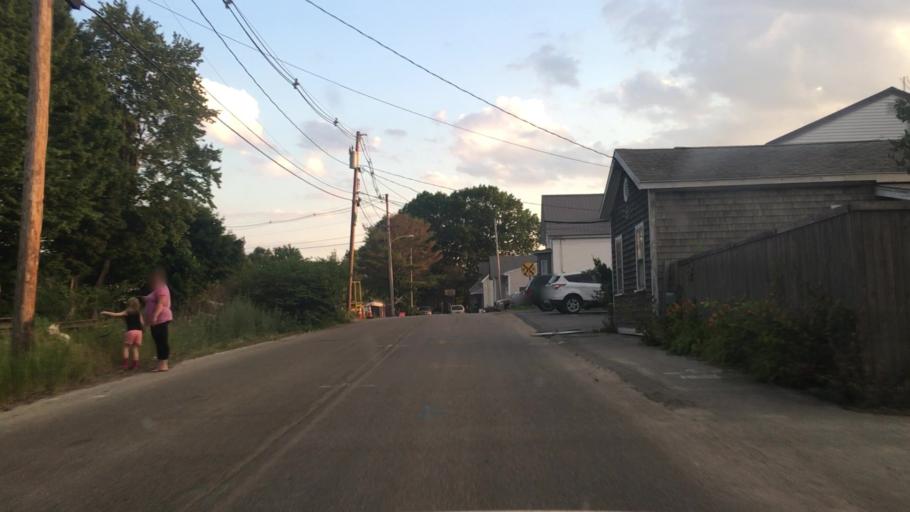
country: US
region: Maine
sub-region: Cumberland County
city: Portland
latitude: 43.6362
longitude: -70.2695
